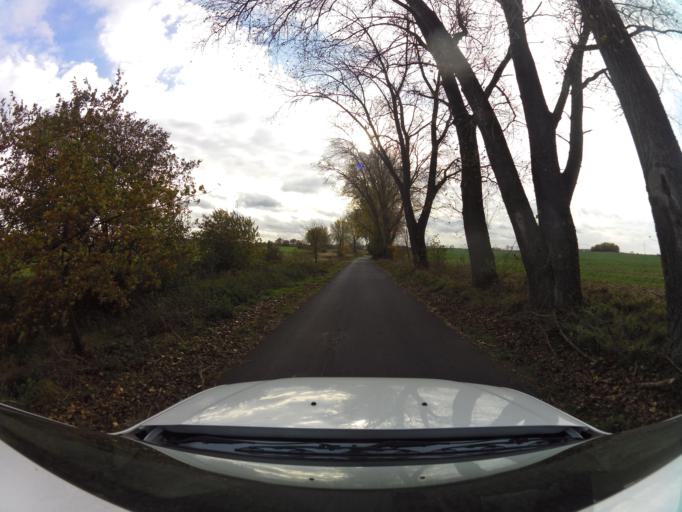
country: PL
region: West Pomeranian Voivodeship
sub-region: Powiat gryficki
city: Gryfice
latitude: 53.8997
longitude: 15.1303
